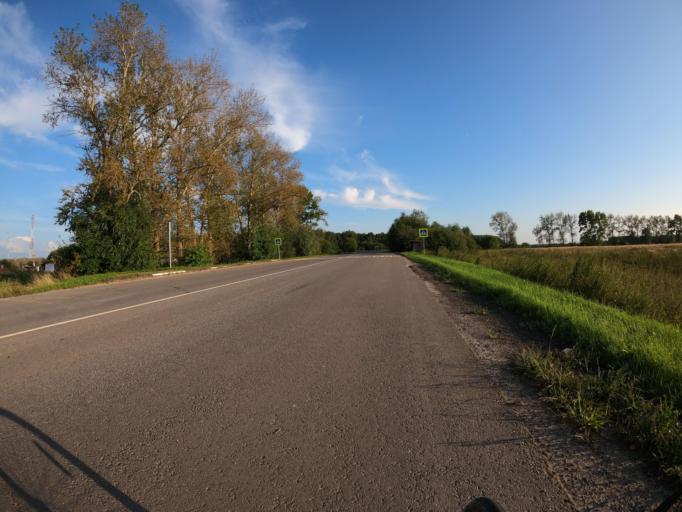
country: RU
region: Moskovskaya
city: Meshcherino
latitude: 55.1132
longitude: 38.3209
